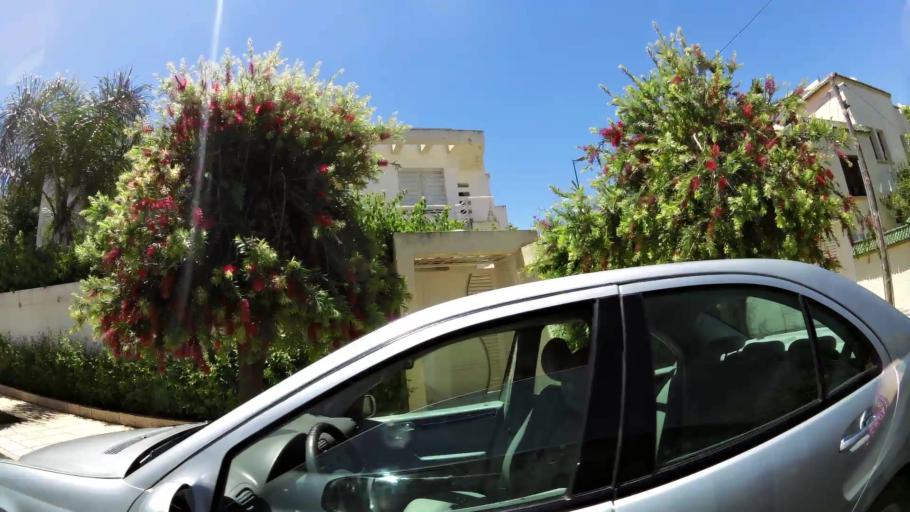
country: MA
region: Meknes-Tafilalet
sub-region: Meknes
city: Meknes
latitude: 33.9058
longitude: -5.5619
